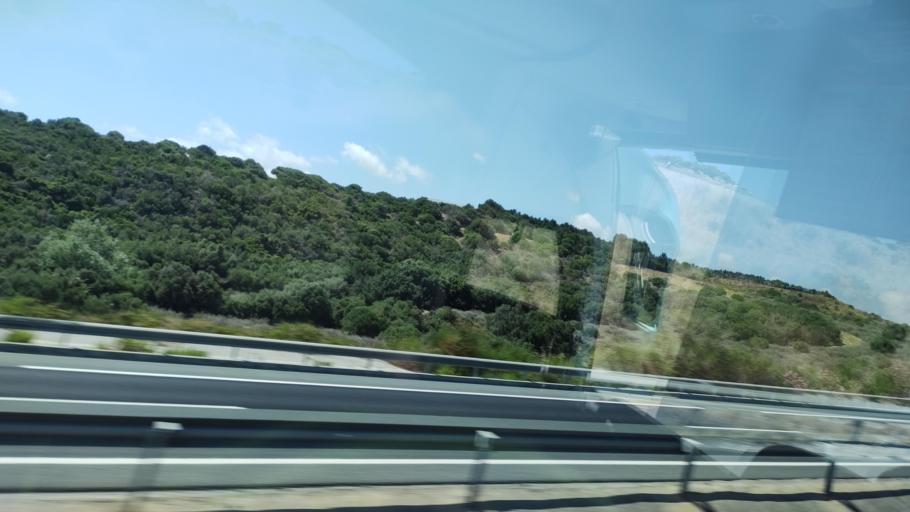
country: ES
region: Andalusia
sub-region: Provincia de Malaga
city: Manilva
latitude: 36.3020
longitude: -5.2793
